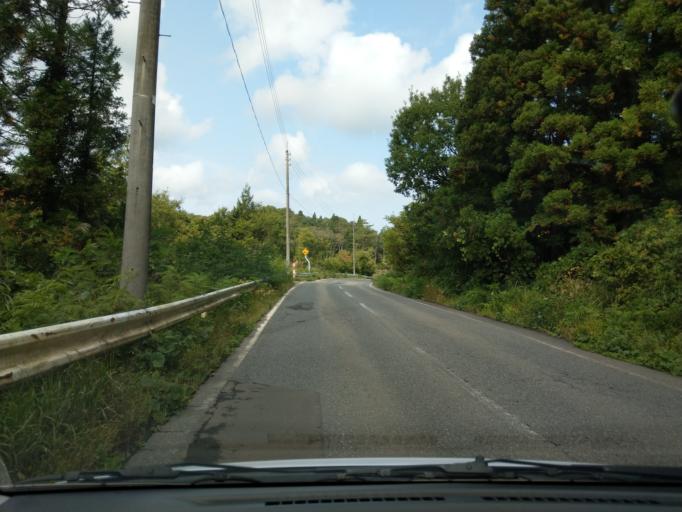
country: JP
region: Akita
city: Omagari
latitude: 39.4615
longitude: 140.3175
